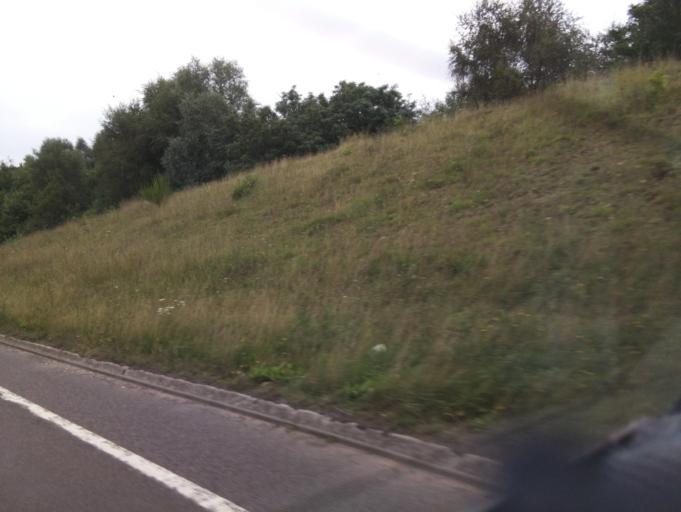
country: GB
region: England
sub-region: Shropshire
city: Stoke upon Tern
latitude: 52.8578
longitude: -2.5556
